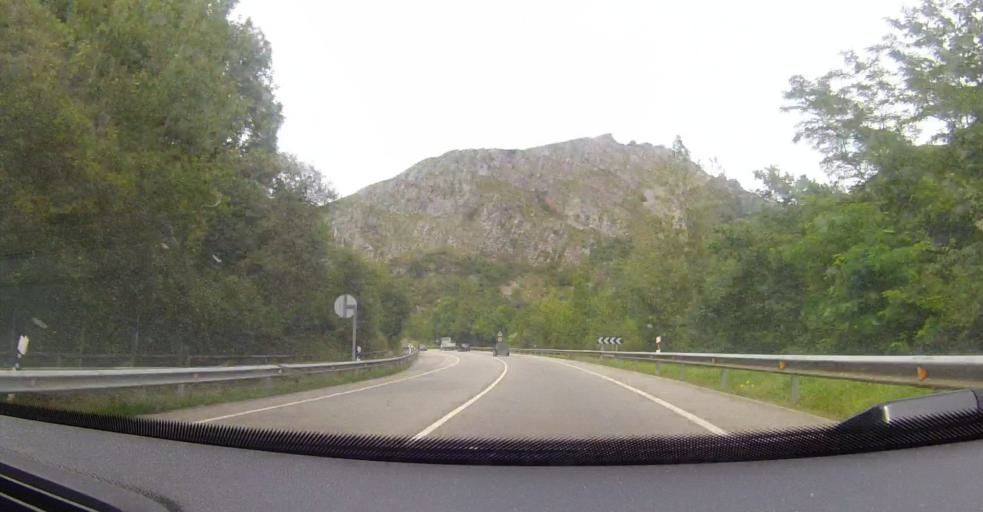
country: ES
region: Asturias
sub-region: Province of Asturias
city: Parres
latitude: 43.3689
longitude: -5.1495
